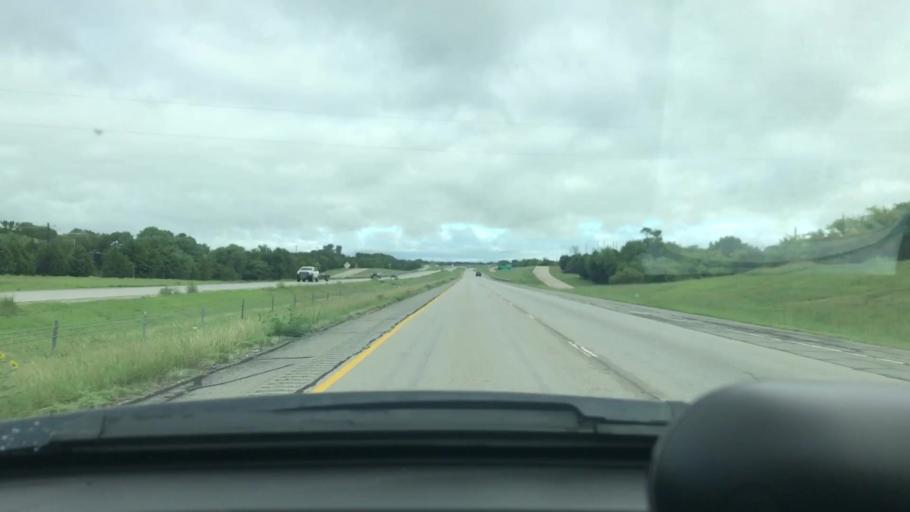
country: US
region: Texas
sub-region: Grayson County
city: Van Alstyne
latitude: 33.3862
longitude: -96.5806
